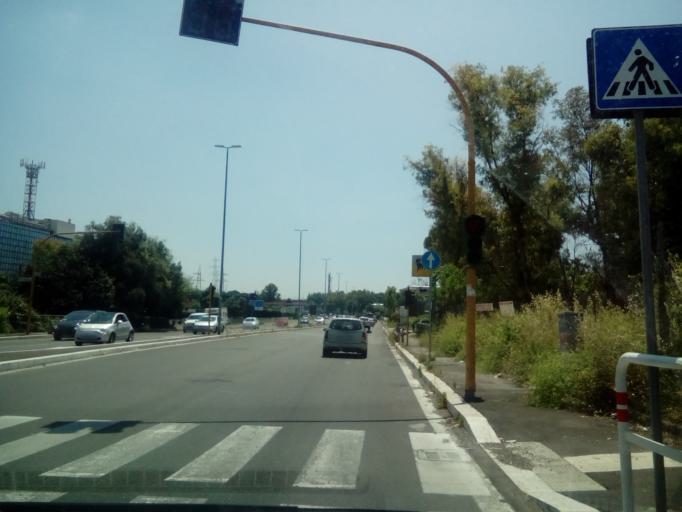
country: IT
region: Latium
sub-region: Citta metropolitana di Roma Capitale
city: Selcetta
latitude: 41.8035
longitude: 12.4819
